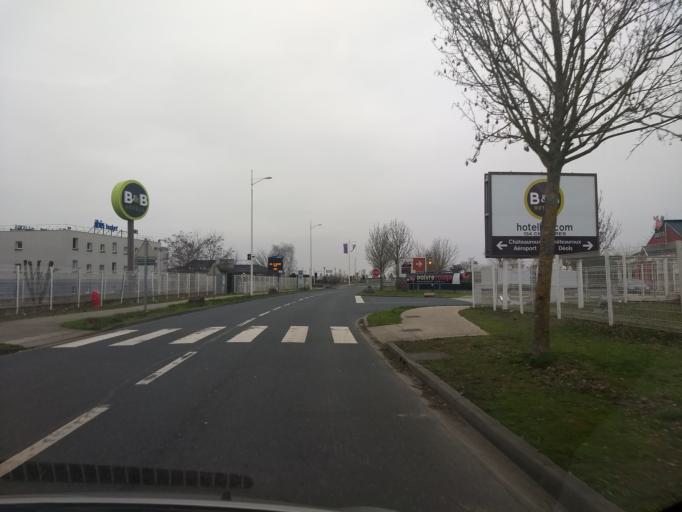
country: FR
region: Centre
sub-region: Departement de l'Indre
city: Deols
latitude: 46.8516
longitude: 1.7047
